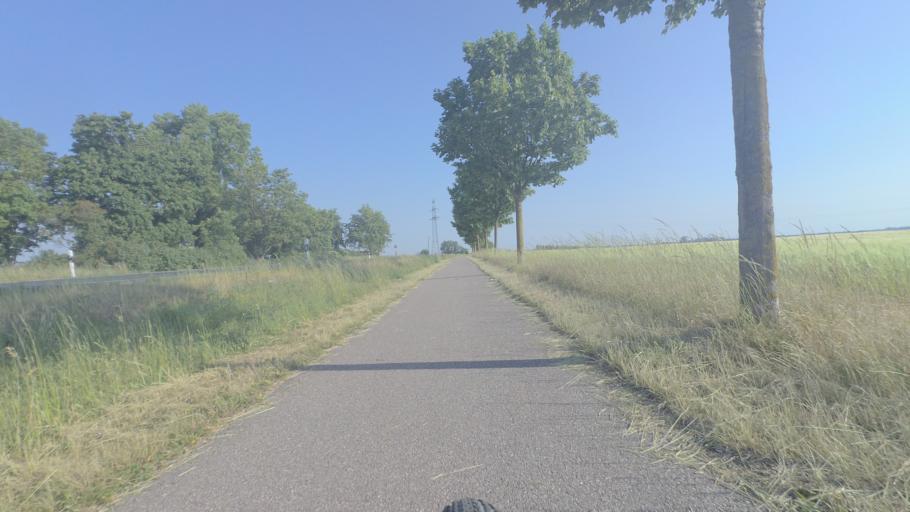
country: DE
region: Saxony-Anhalt
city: Osternienburger Land
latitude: 51.7726
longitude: 11.9999
